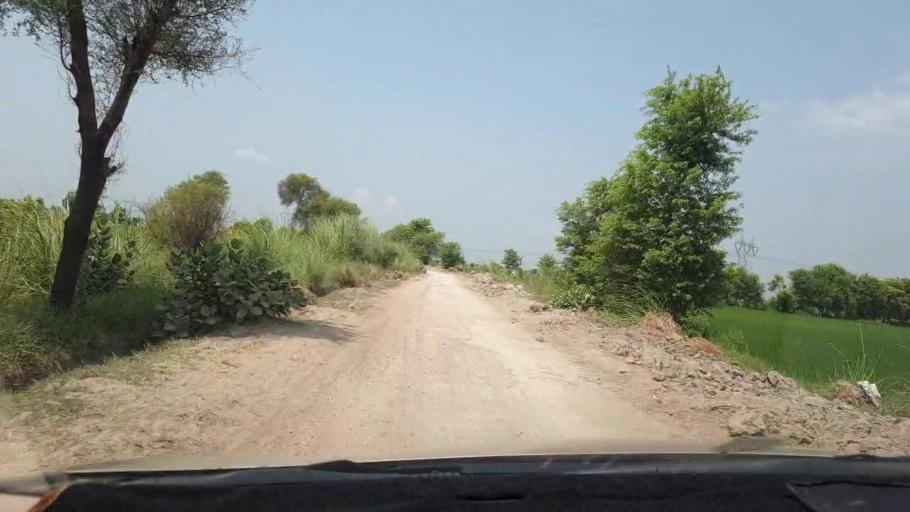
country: PK
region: Sindh
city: Naudero
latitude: 27.6646
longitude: 68.3111
